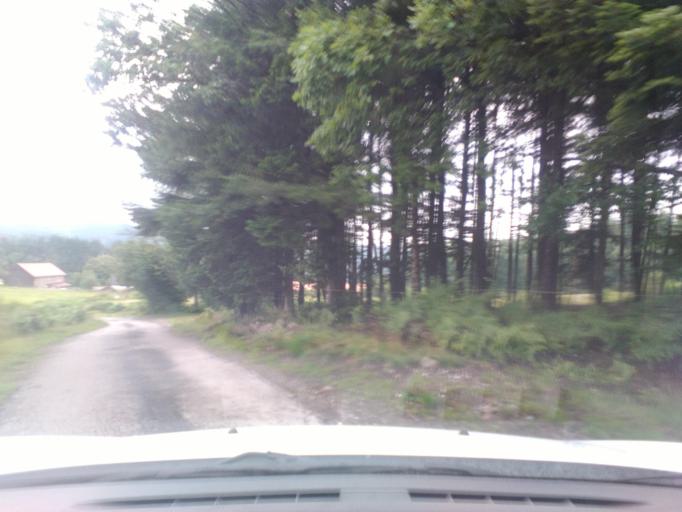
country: FR
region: Lorraine
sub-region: Departement des Vosges
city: Le Tholy
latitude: 48.1200
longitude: 6.7028
